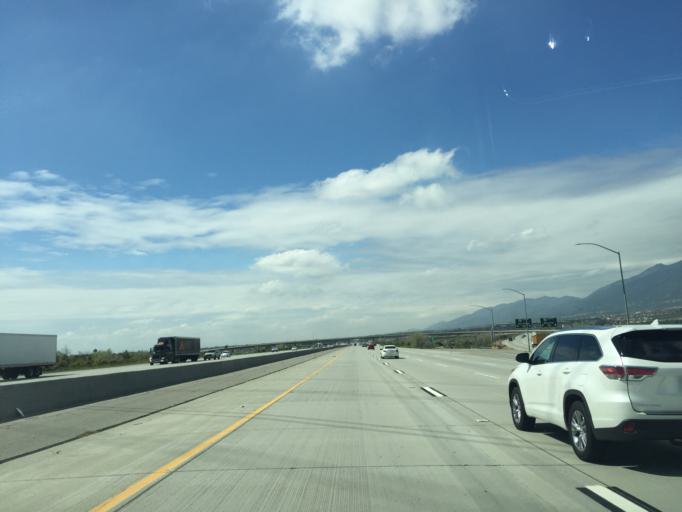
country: US
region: California
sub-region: San Bernardino County
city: Fontana
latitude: 34.1365
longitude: -117.4836
